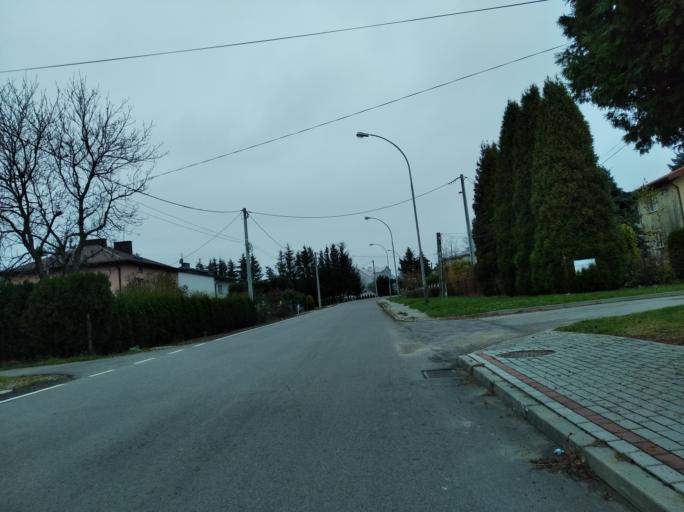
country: PL
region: Subcarpathian Voivodeship
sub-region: Powiat krosnienski
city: Jedlicze
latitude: 49.7212
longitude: 21.6510
